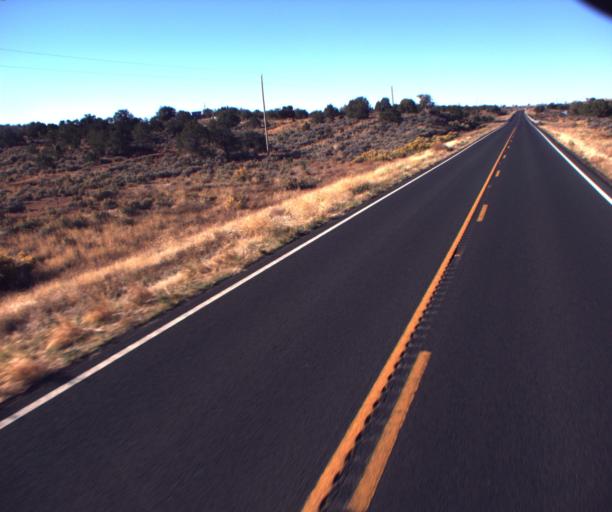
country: US
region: Arizona
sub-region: Apache County
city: Ganado
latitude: 35.7654
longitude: -109.7486
